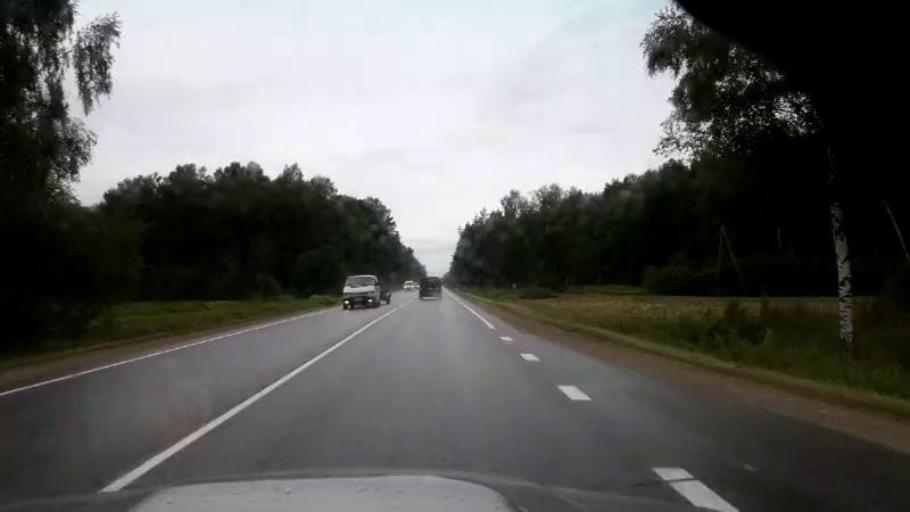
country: LV
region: Kekava
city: Kekava
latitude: 56.8129
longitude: 24.2592
